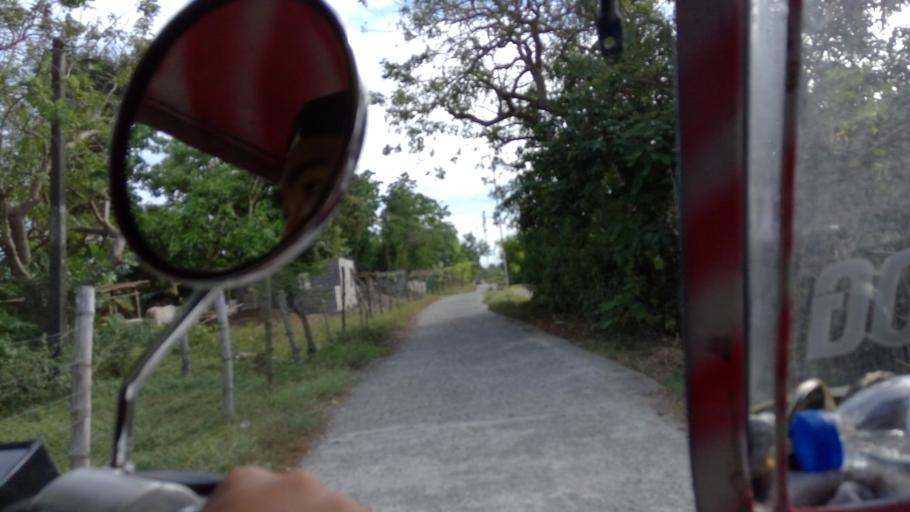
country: PH
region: Ilocos
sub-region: Province of La Union
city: San Eugenio
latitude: 16.3714
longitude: 120.3523
